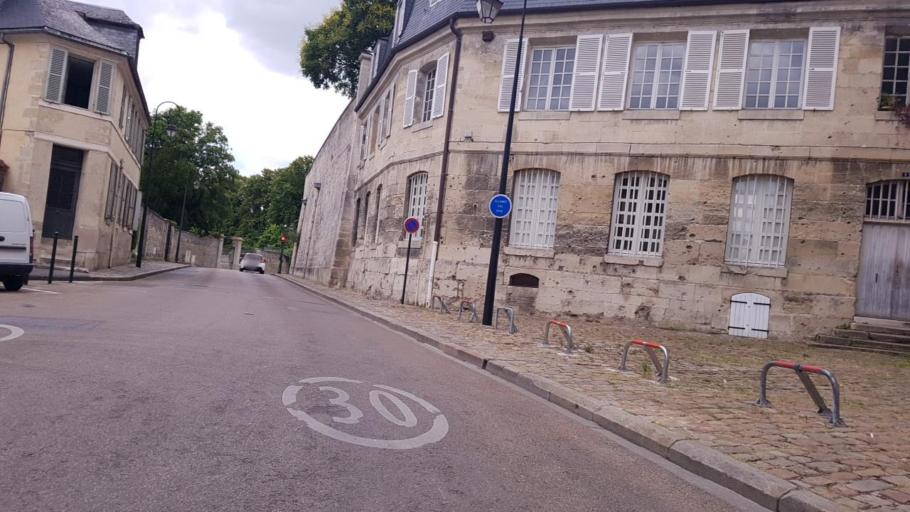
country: FR
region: Picardie
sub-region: Departement de l'Oise
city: Compiegne
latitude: 49.4203
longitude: 2.8317
